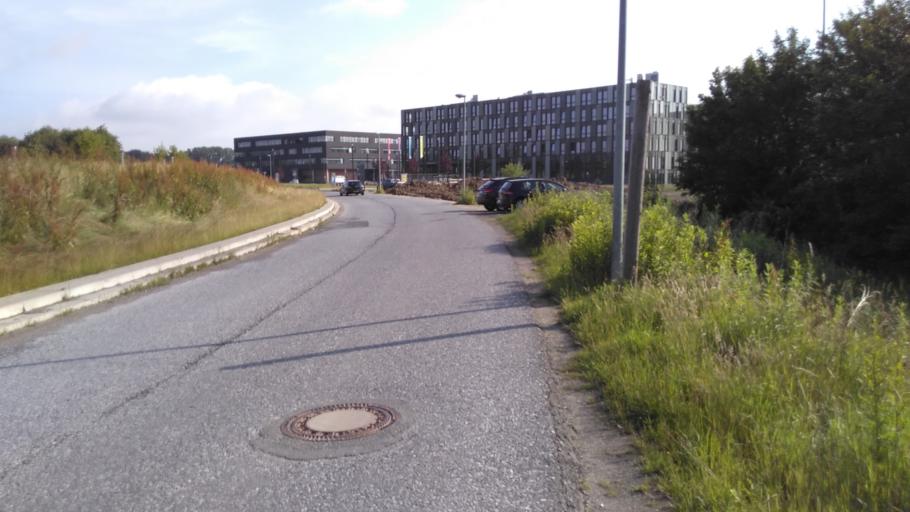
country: DE
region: North Rhine-Westphalia
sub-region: Regierungsbezirk Detmold
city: Bielefeld
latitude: 52.0427
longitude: 8.4912
